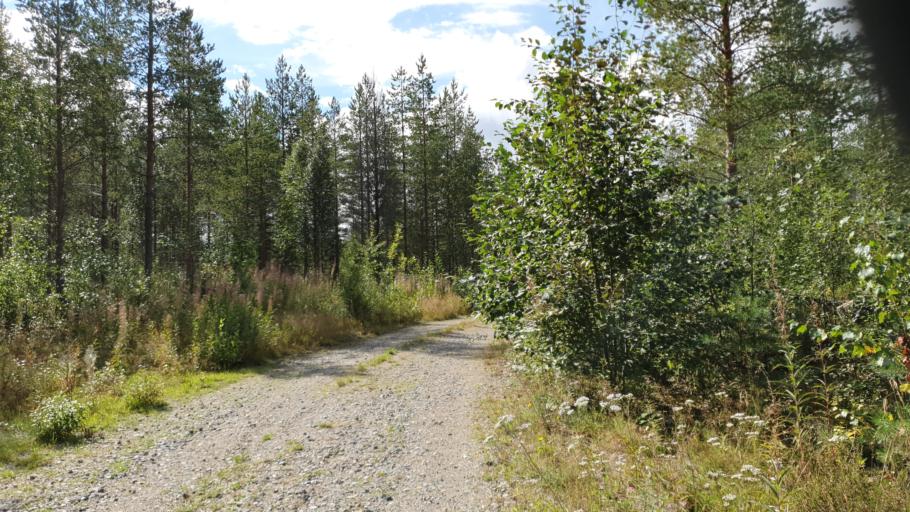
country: FI
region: Kainuu
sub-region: Kehys-Kainuu
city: Kuhmo
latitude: 64.1452
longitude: 29.3873
